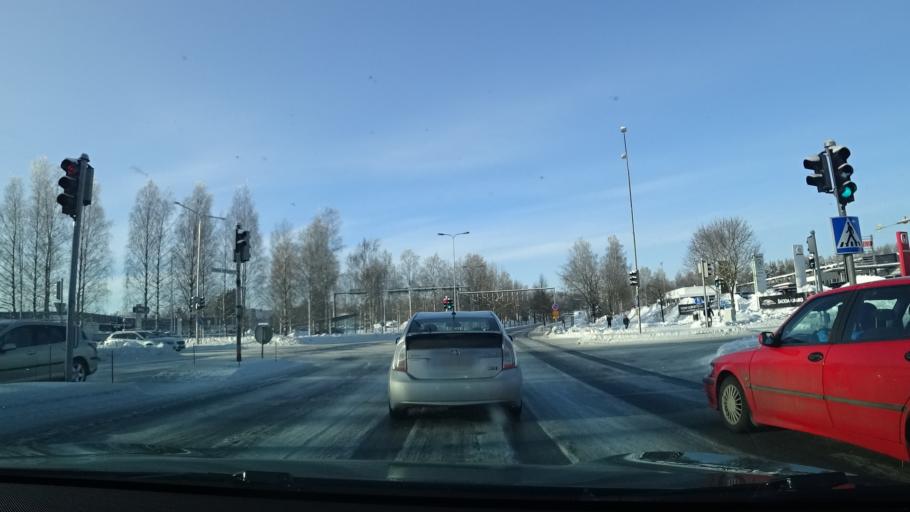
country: FI
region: South Karelia
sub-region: Lappeenranta
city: Lappeenranta
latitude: 61.0466
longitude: 28.2021
